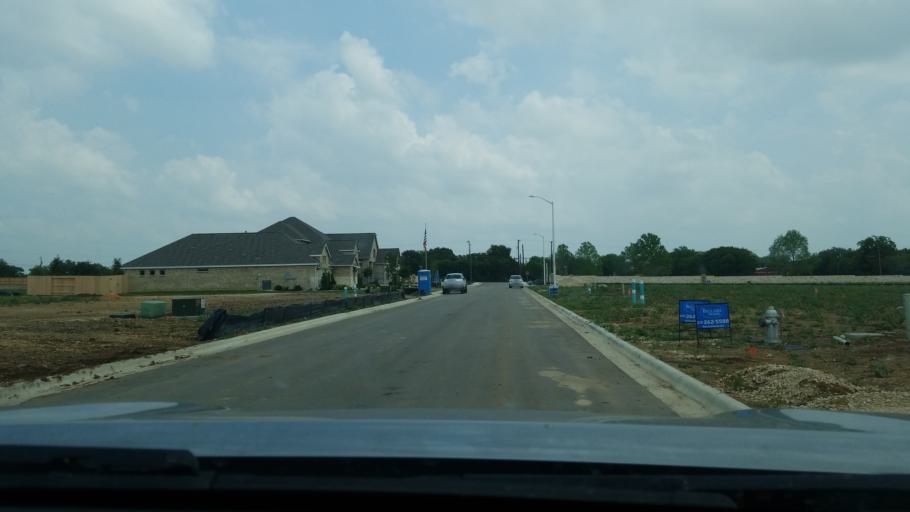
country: US
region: Texas
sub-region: Comal County
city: New Braunfels
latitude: 29.7479
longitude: -98.0959
